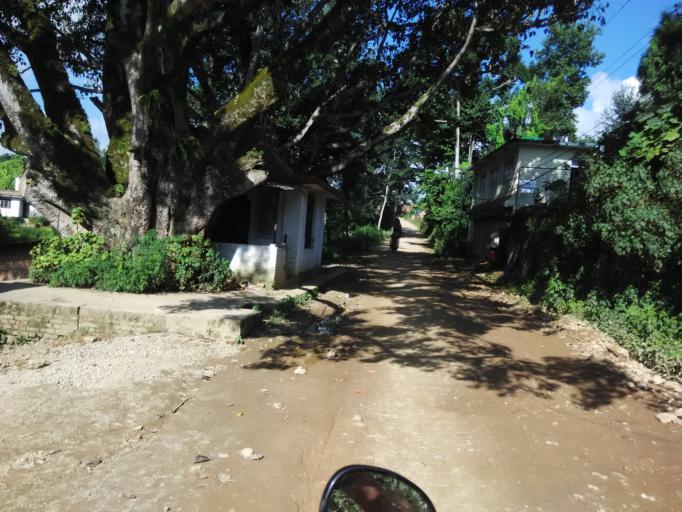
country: NP
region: Central Region
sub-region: Bagmati Zone
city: Patan
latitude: 27.6071
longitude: 85.3418
